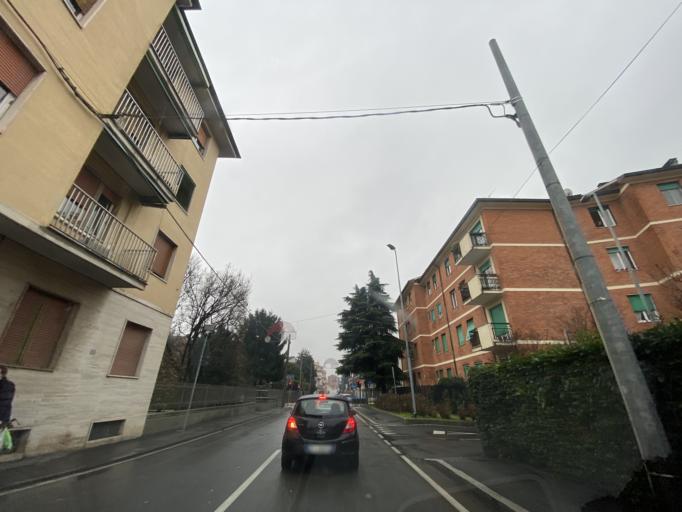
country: IT
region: Lombardy
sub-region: Citta metropolitana di Milano
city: Baranzate
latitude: 45.5295
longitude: 9.1162
